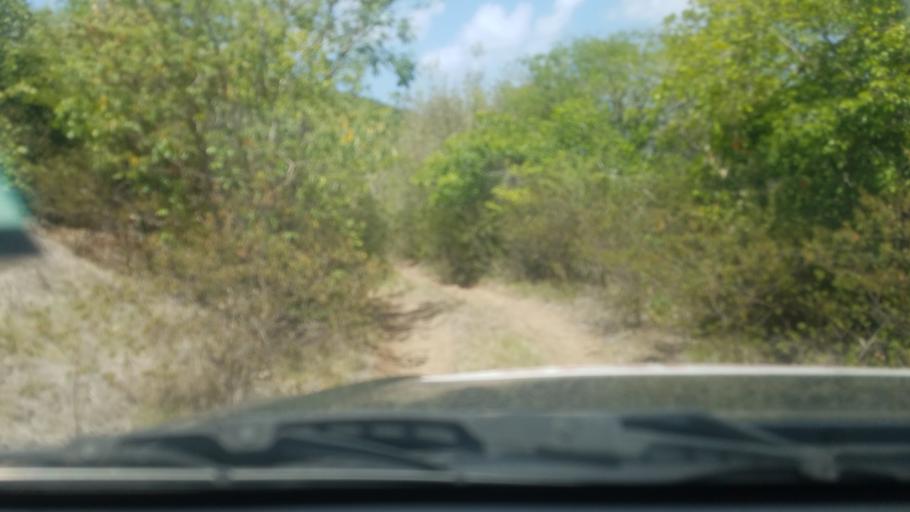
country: LC
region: Vieux-Fort
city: Vieux Fort
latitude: 13.7132
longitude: -60.9534
